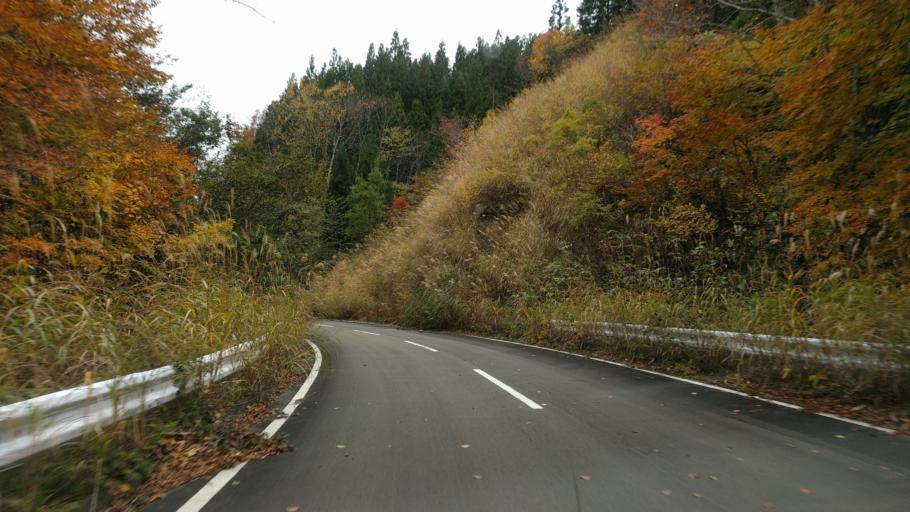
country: JP
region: Fukushima
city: Kitakata
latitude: 37.3798
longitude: 139.7298
